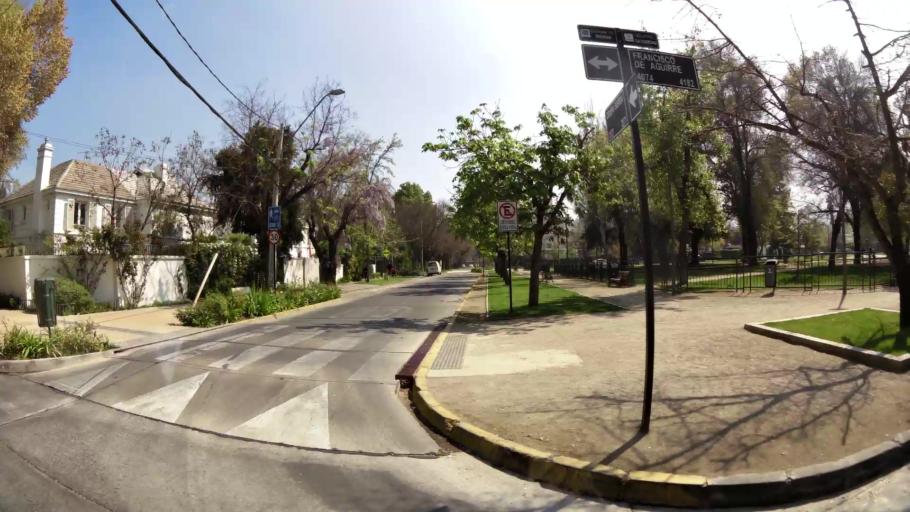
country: CL
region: Santiago Metropolitan
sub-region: Provincia de Santiago
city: Villa Presidente Frei, Nunoa, Santiago, Chile
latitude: -33.3964
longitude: -70.5951
